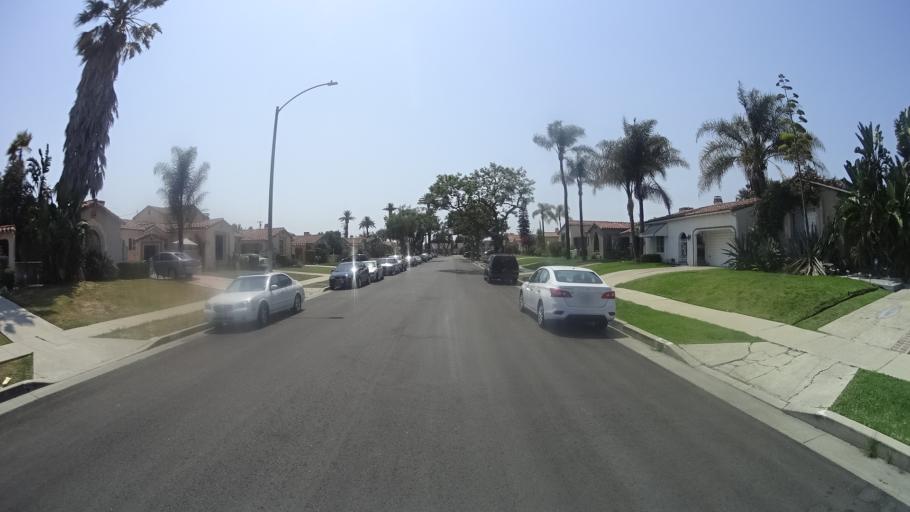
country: US
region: California
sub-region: Los Angeles County
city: View Park-Windsor Hills
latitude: 33.9845
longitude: -118.3367
